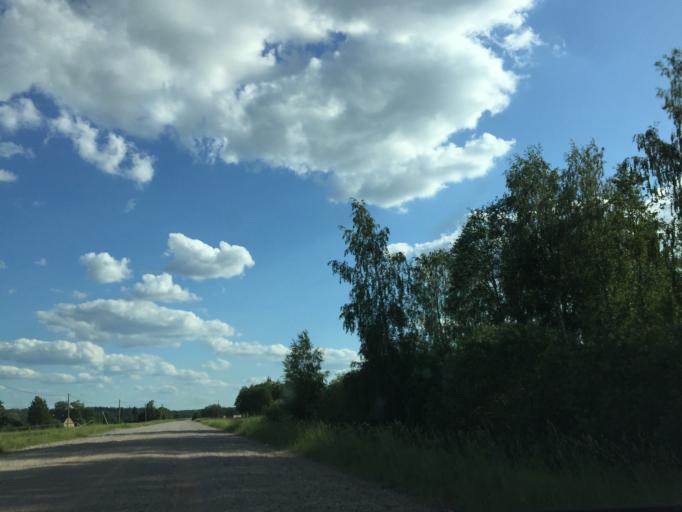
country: LV
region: Kandava
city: Kandava
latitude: 56.9009
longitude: 22.7914
